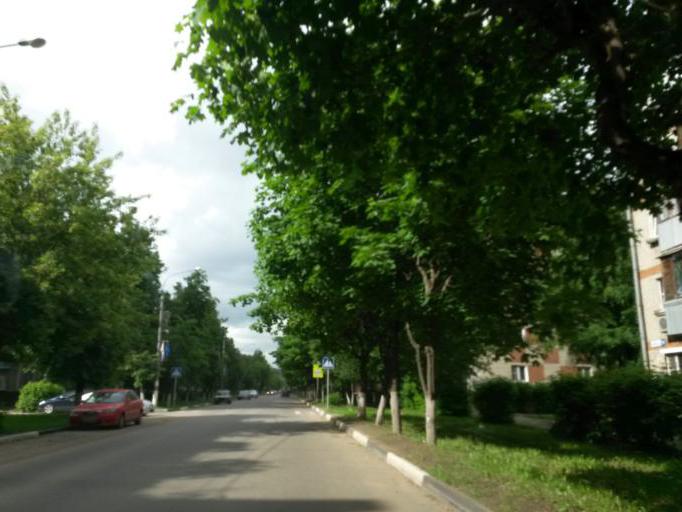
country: RU
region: Moskovskaya
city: Klimovsk
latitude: 55.3759
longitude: 37.5405
